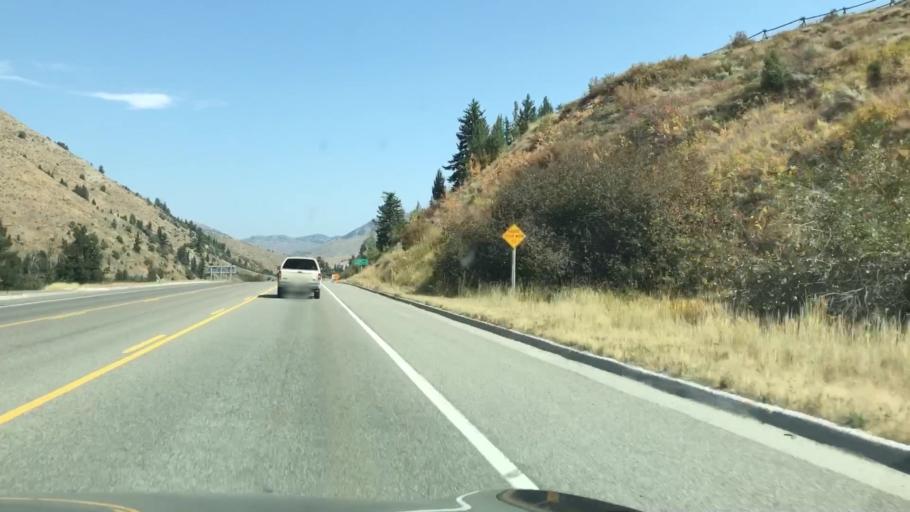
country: US
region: Wyoming
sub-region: Teton County
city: Hoback
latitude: 43.3252
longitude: -110.7297
